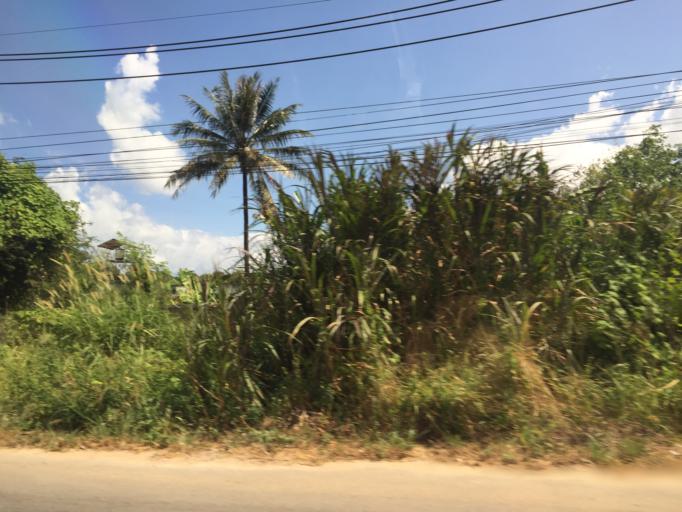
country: TH
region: Krabi
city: Krabi
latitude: 8.1006
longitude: 98.8875
